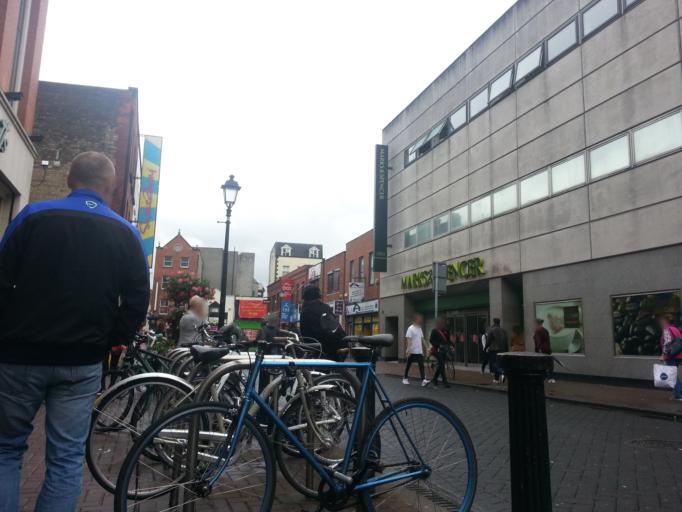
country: IE
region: Leinster
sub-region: Dublin City
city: Dublin
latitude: 53.3485
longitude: -6.2641
